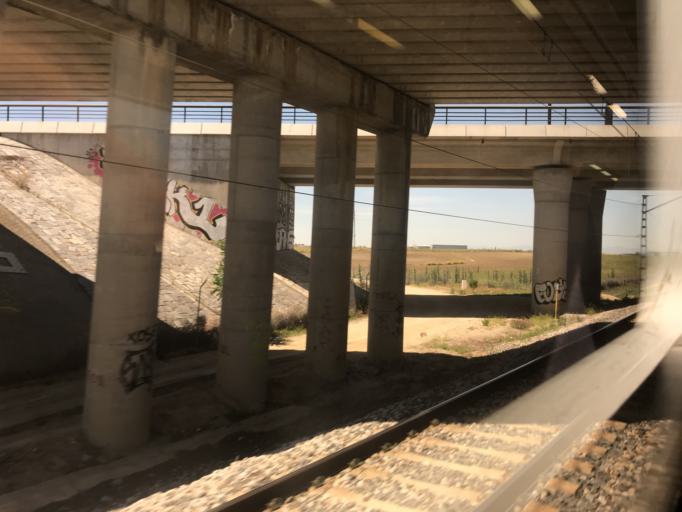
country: ES
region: Madrid
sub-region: Provincia de Madrid
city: Getafe
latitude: 40.2814
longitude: -3.7041
